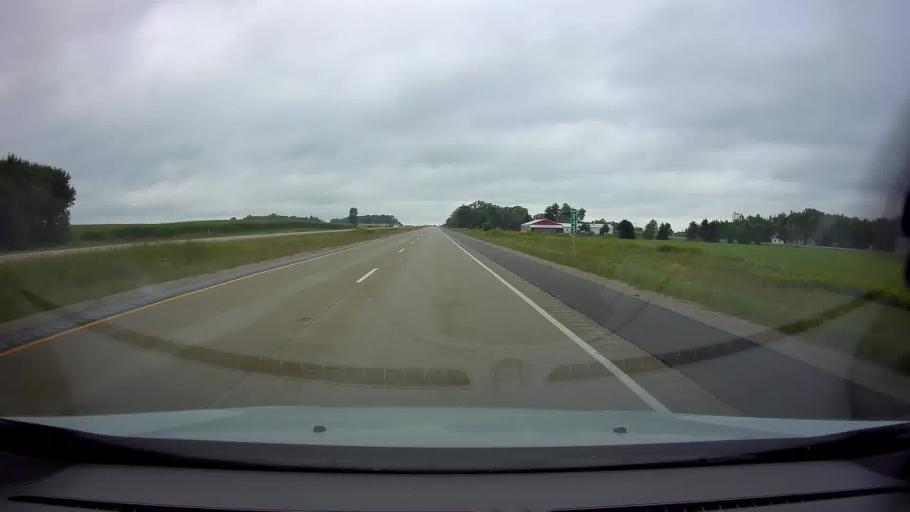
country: US
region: Wisconsin
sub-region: Brown County
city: Pulaski
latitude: 44.6373
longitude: -88.2853
